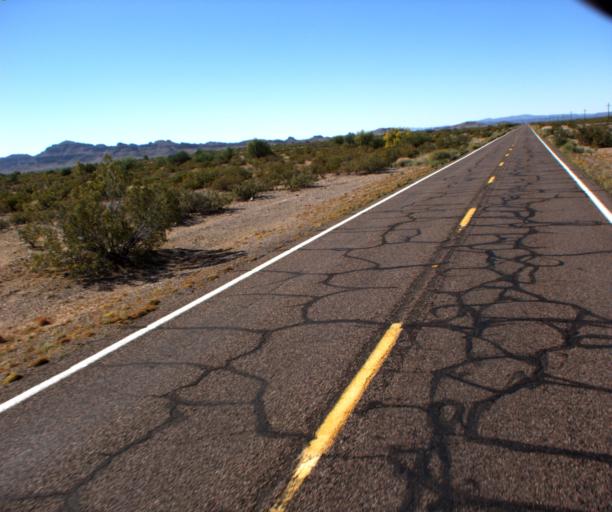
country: US
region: Arizona
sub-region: Maricopa County
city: Gila Bend
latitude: 32.7376
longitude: -112.8322
